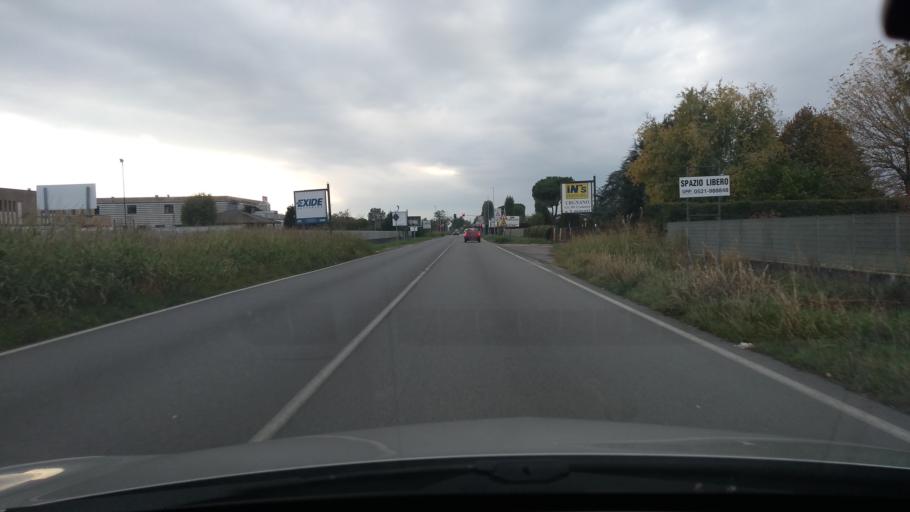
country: IT
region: Lombardy
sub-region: Provincia di Bergamo
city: Ghisalba
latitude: 45.5896
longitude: 9.7550
